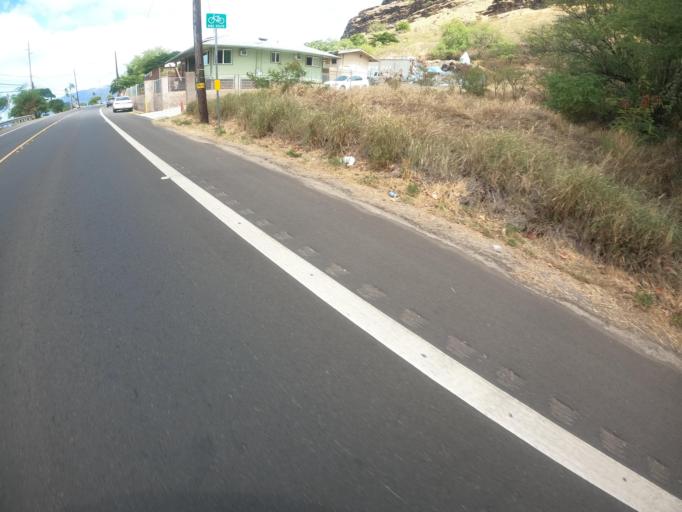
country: US
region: Hawaii
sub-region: Honolulu County
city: Makaha
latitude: 21.4850
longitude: -158.2292
